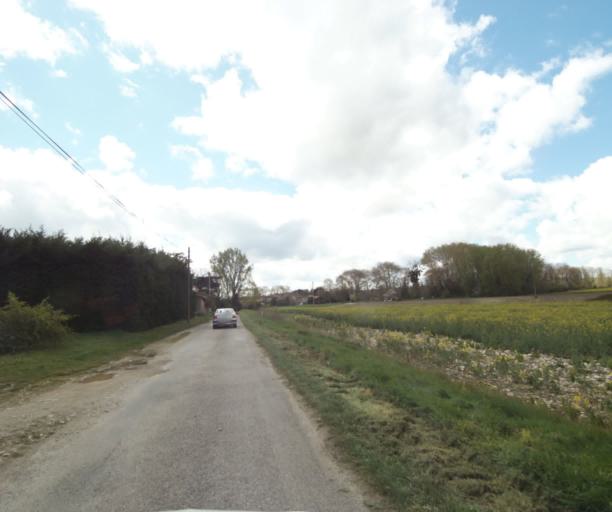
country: FR
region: Midi-Pyrenees
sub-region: Departement de l'Ariege
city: Saverdun
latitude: 43.2622
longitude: 1.5835
